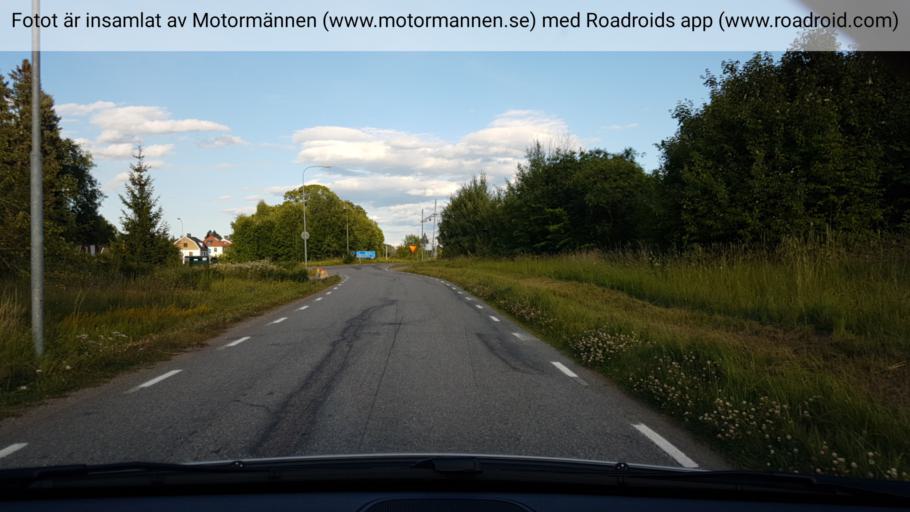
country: SE
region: Vaestmanland
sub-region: Vasteras
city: Tillberga
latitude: 59.6890
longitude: 16.6124
